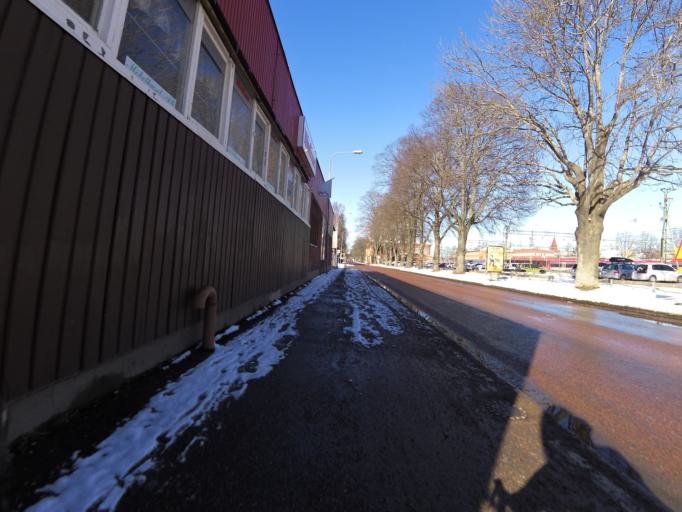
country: SE
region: Gaevleborg
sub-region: Gavle Kommun
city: Gavle
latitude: 60.6707
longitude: 17.1562
